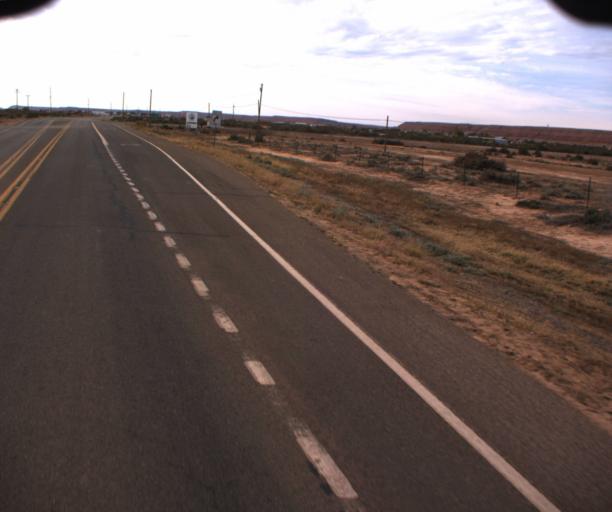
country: US
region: Arizona
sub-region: Apache County
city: Many Farms
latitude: 36.3655
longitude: -109.6138
